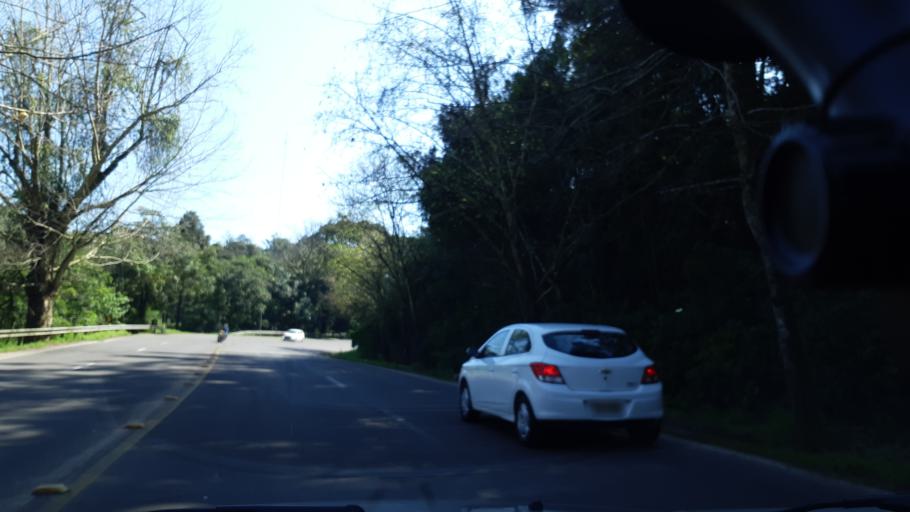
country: BR
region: Rio Grande do Sul
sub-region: Nova Petropolis
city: Nova Petropolis
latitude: -29.3884
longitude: -51.1259
